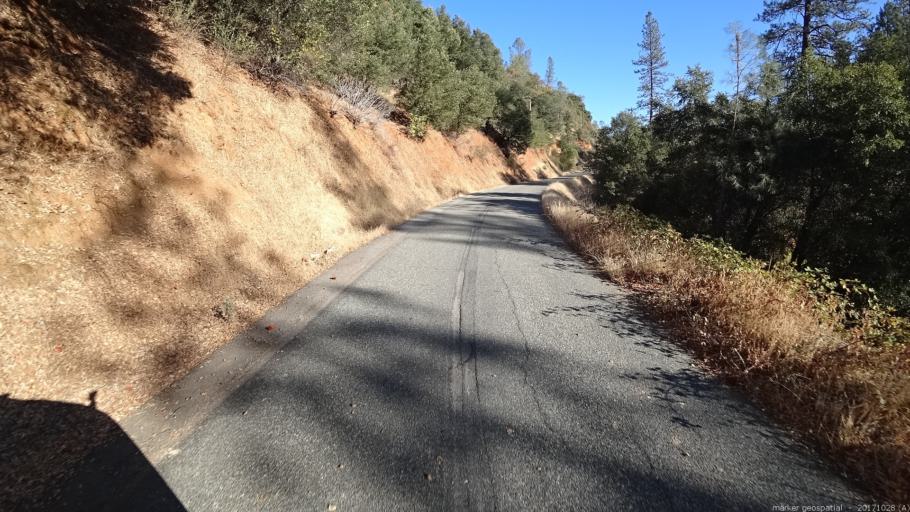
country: US
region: California
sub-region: Trinity County
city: Lewiston
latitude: 40.6555
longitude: -122.6650
